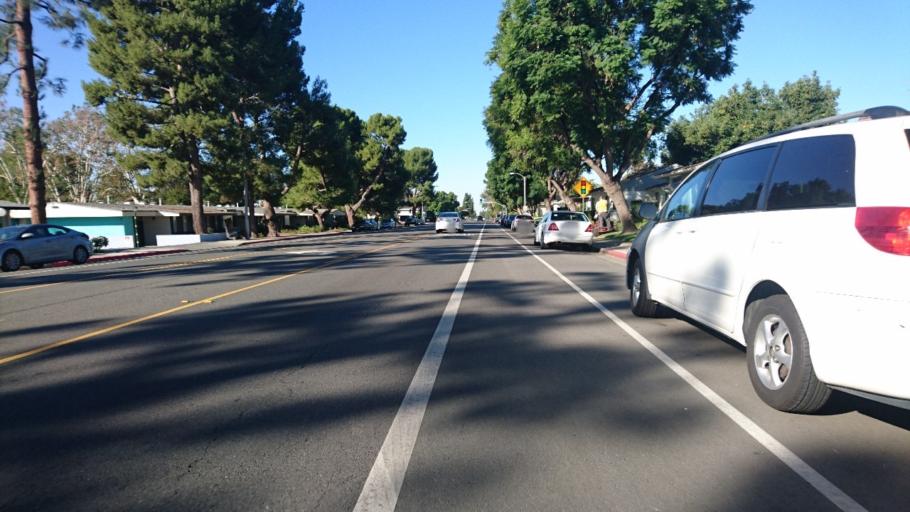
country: US
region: California
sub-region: Los Angeles County
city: Claremont
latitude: 34.0965
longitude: -117.7255
